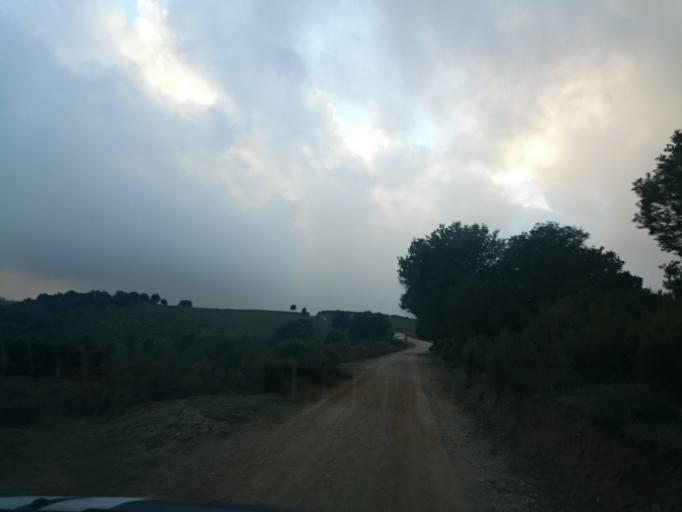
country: ES
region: Catalonia
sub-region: Provincia de Barcelona
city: Seva
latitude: 41.7883
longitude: 2.3330
